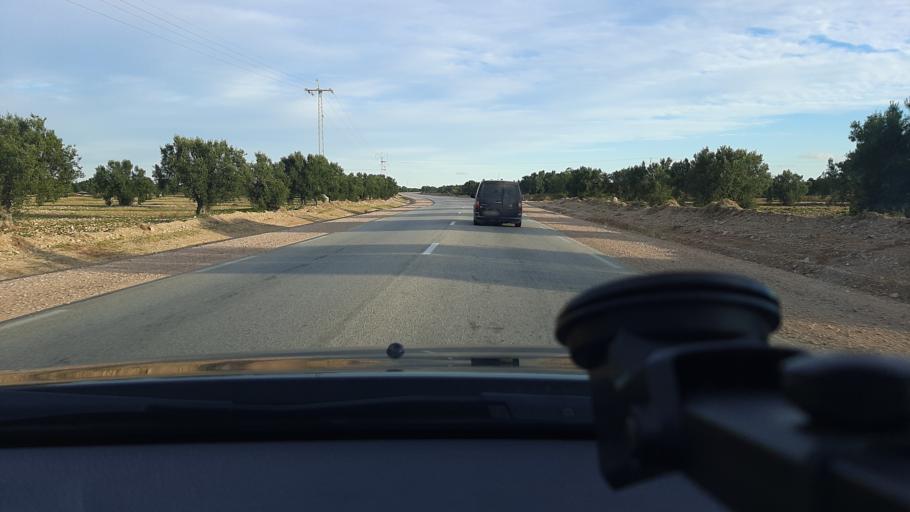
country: TN
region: Safaqis
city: Sfax
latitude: 34.9189
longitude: 10.4540
